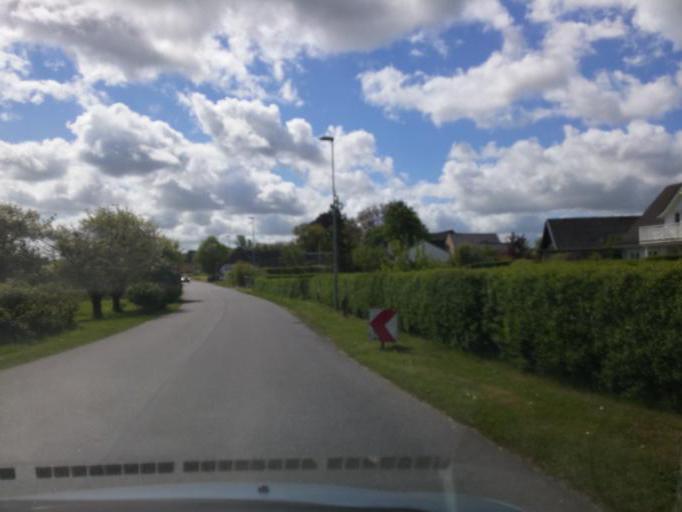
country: DK
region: South Denmark
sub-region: Kerteminde Kommune
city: Munkebo
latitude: 55.4435
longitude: 10.5408
